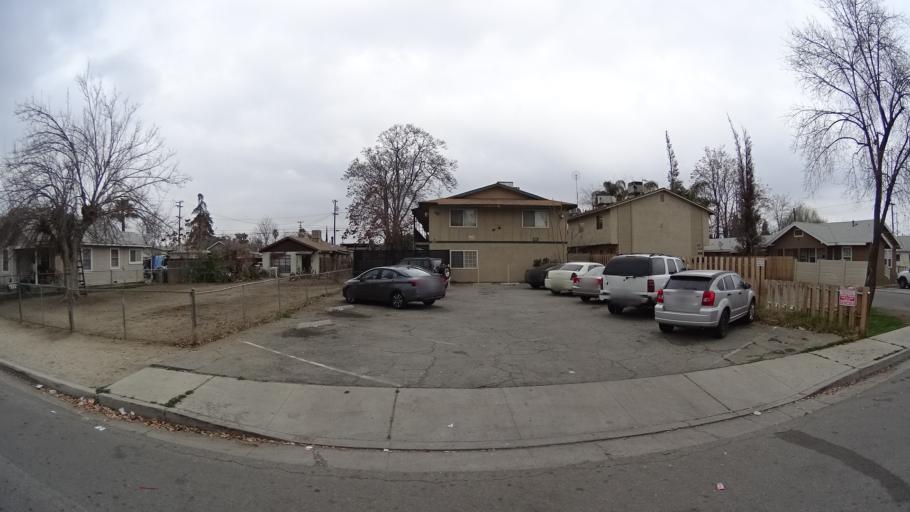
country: US
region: California
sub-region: Kern County
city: Bakersfield
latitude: 35.3851
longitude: -119.0080
